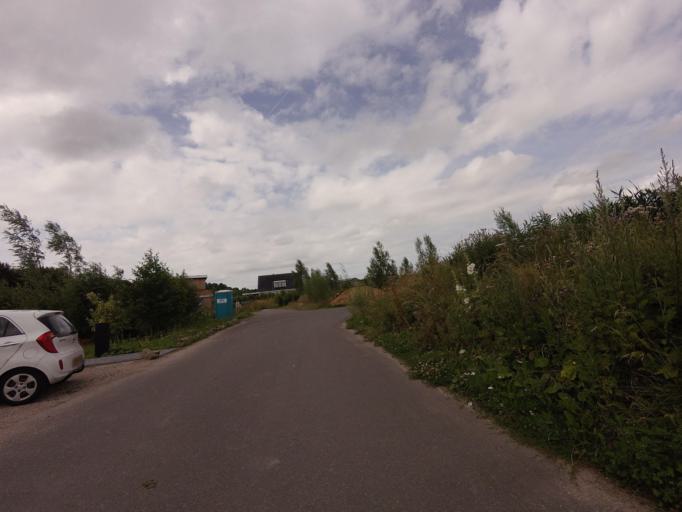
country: NL
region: North Holland
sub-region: Gemeente Huizen
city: Huizen
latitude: 52.3313
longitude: 5.3148
